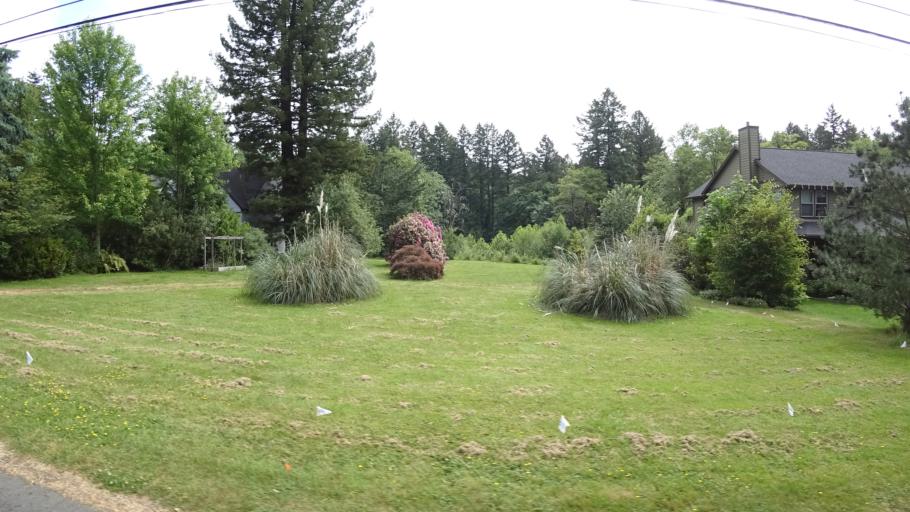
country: US
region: Oregon
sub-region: Clackamas County
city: Lake Oswego
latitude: 45.4474
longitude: -122.6834
